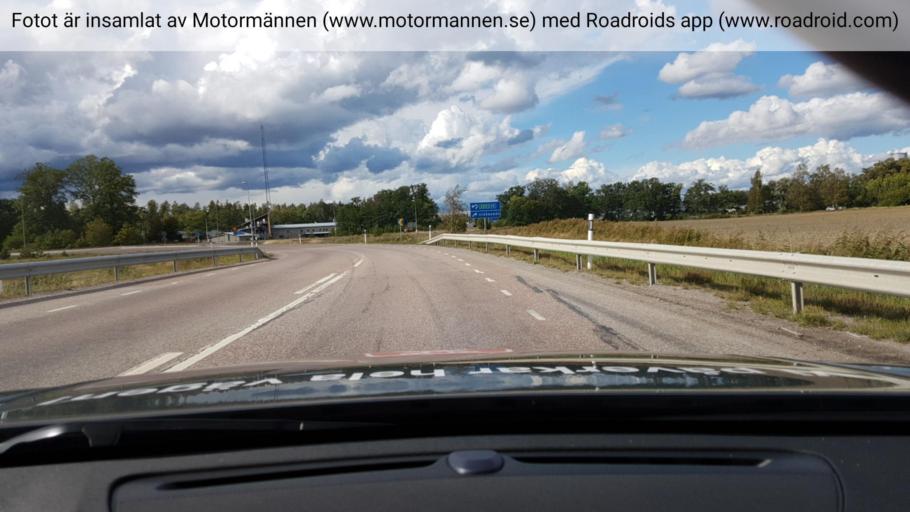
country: SE
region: Soedermanland
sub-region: Strangnas Kommun
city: Strangnas
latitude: 59.3427
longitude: 17.0364
